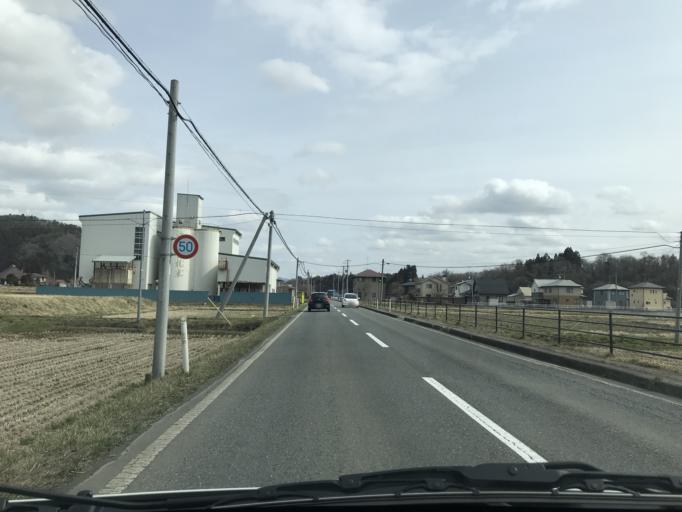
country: JP
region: Iwate
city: Mizusawa
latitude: 39.2062
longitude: 141.1946
